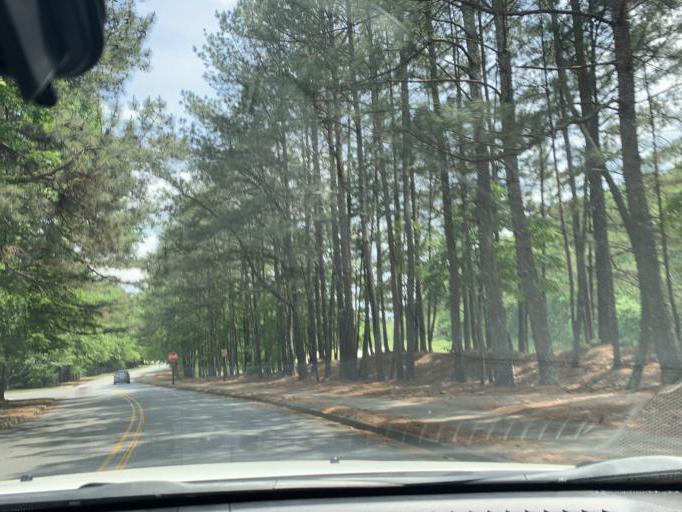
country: US
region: Georgia
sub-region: Forsyth County
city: Cumming
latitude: 34.1474
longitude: -84.1323
